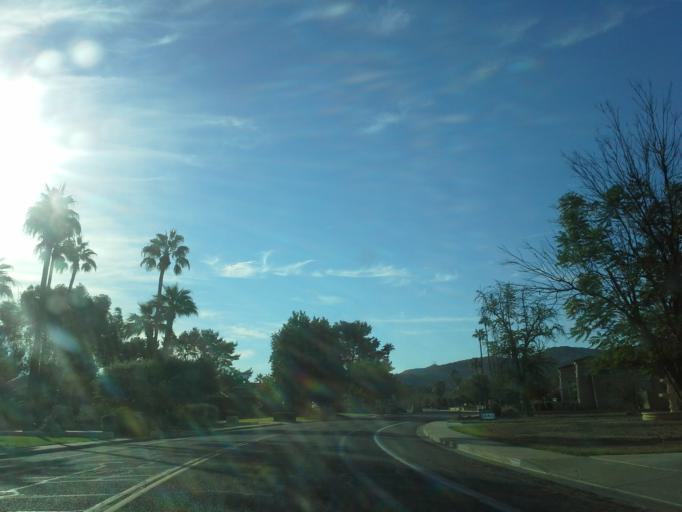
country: US
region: Arizona
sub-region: Maricopa County
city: Glendale
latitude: 33.6192
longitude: -112.0869
